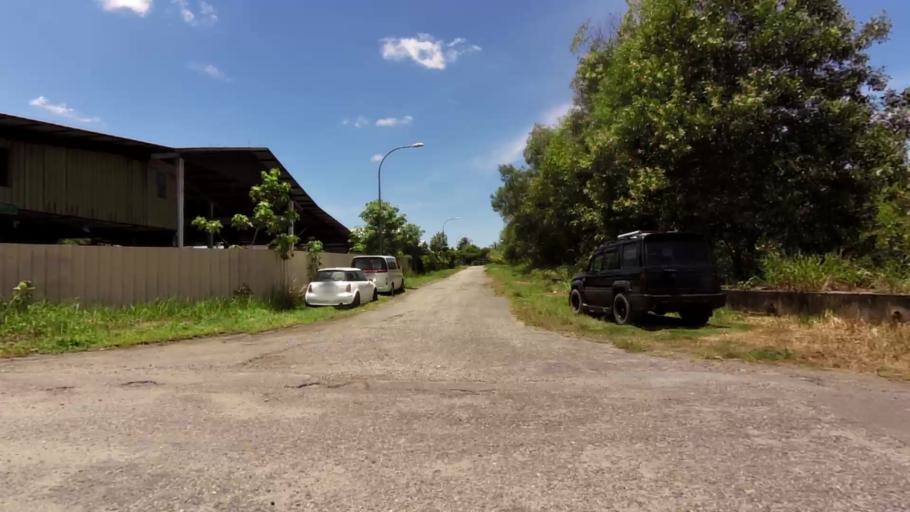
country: BN
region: Brunei and Muara
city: Bandar Seri Begawan
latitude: 4.9398
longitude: 114.9571
